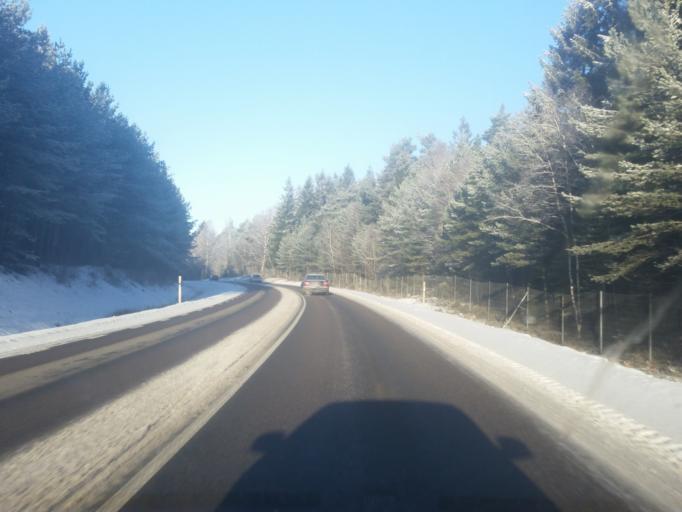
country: SE
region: Vaestra Goetaland
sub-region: Partille Kommun
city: Furulund
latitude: 57.7093
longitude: 12.1514
